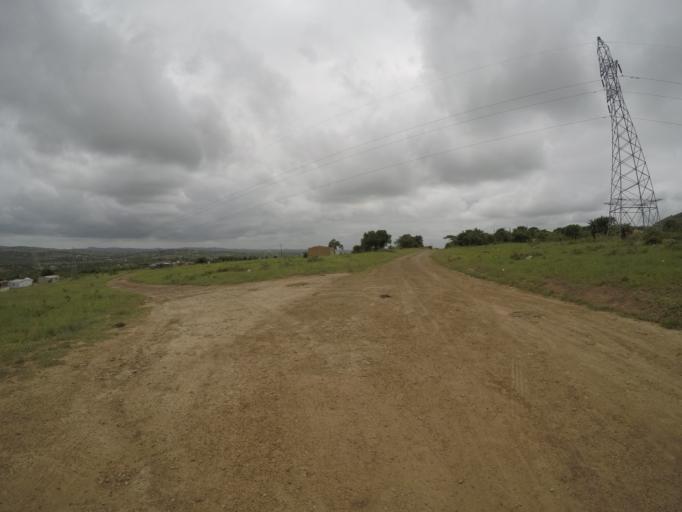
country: ZA
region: KwaZulu-Natal
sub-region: uThungulu District Municipality
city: Empangeni
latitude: -28.6008
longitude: 31.8468
